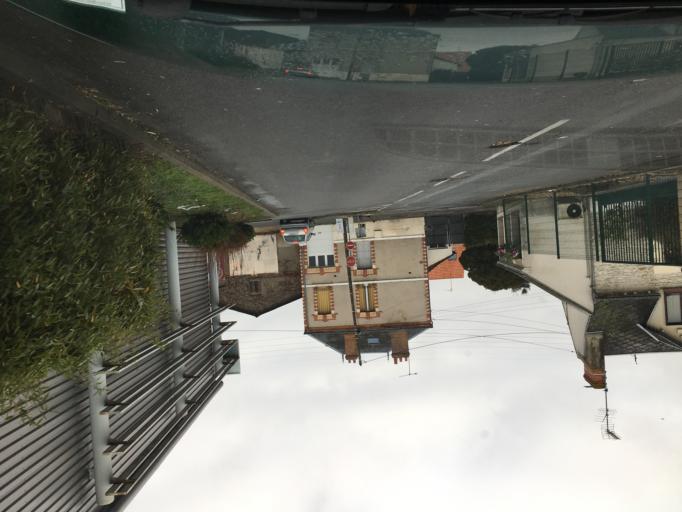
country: FR
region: Centre
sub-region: Departement du Loiret
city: Saint-Jean-le-Blanc
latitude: 47.8787
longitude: 1.9088
